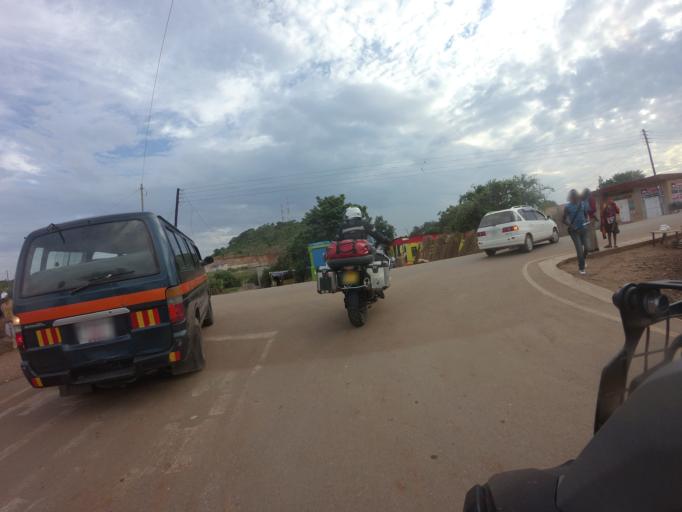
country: ZM
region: Lusaka
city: Lusaka
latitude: -15.5403
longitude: 28.2388
